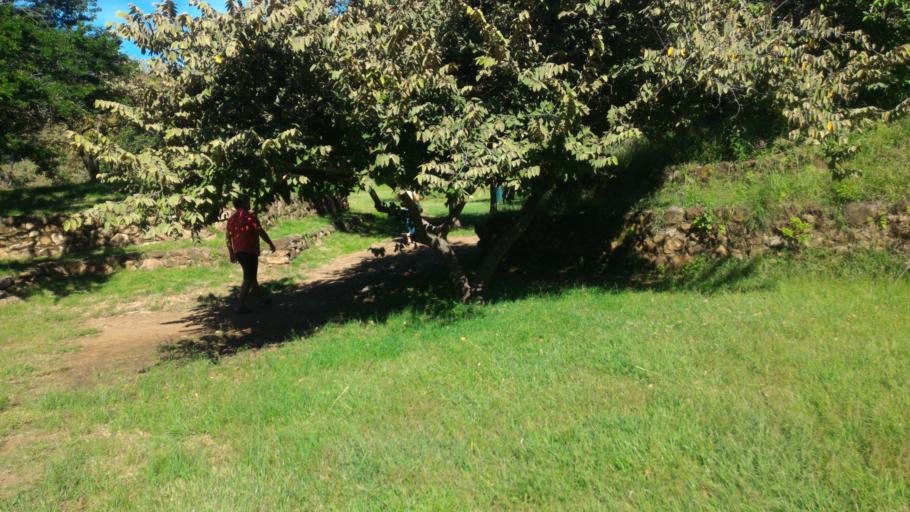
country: MX
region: Jalisco
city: Teuchitlan
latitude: 20.6942
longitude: -103.8363
